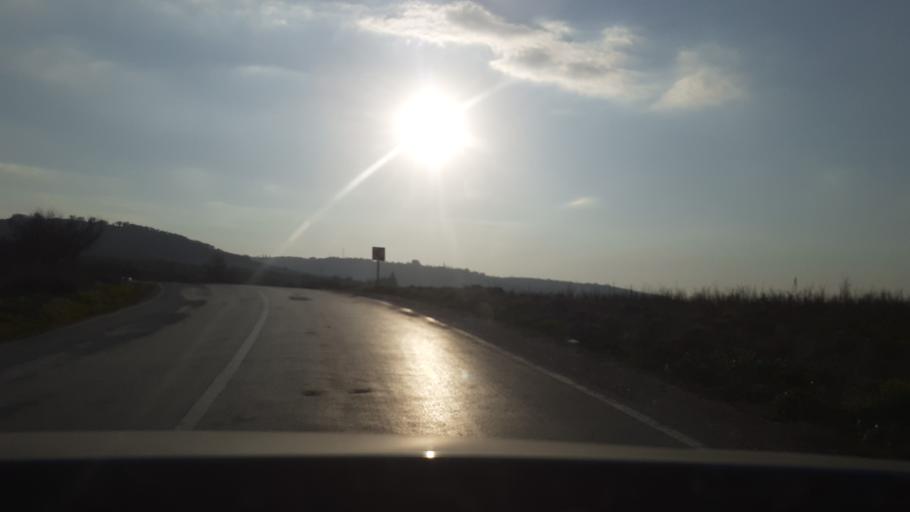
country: TR
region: Hatay
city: Oymakli
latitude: 36.1124
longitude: 36.2794
